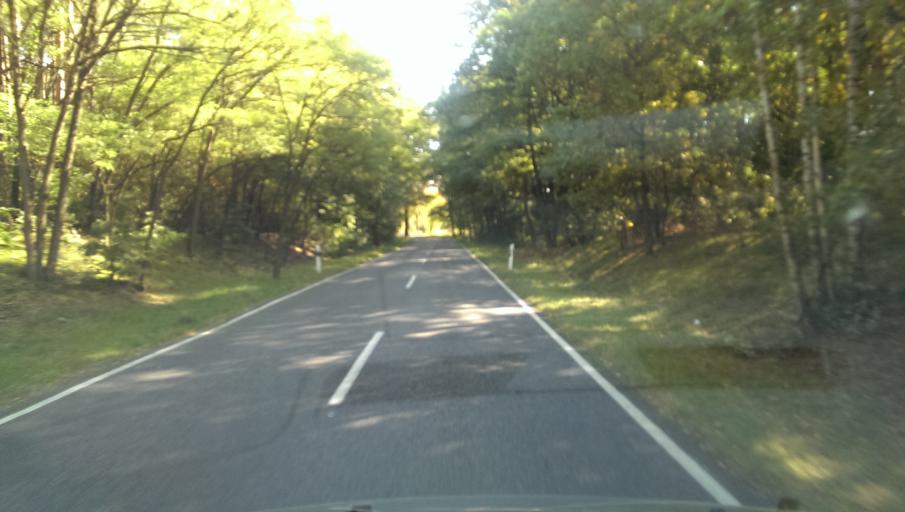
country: DE
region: Brandenburg
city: Halbe
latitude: 52.0971
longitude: 13.7103
